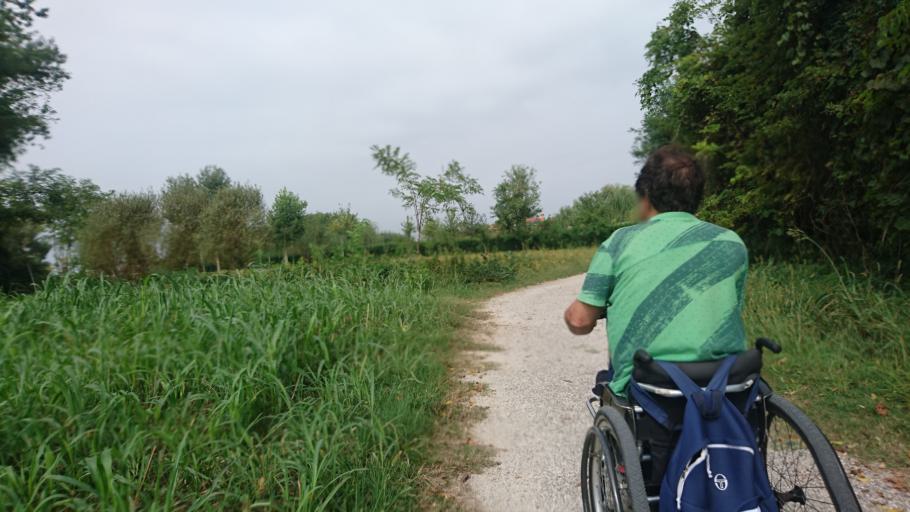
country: IT
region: Veneto
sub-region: Provincia di Padova
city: Grantorto
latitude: 45.5761
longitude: 11.7570
